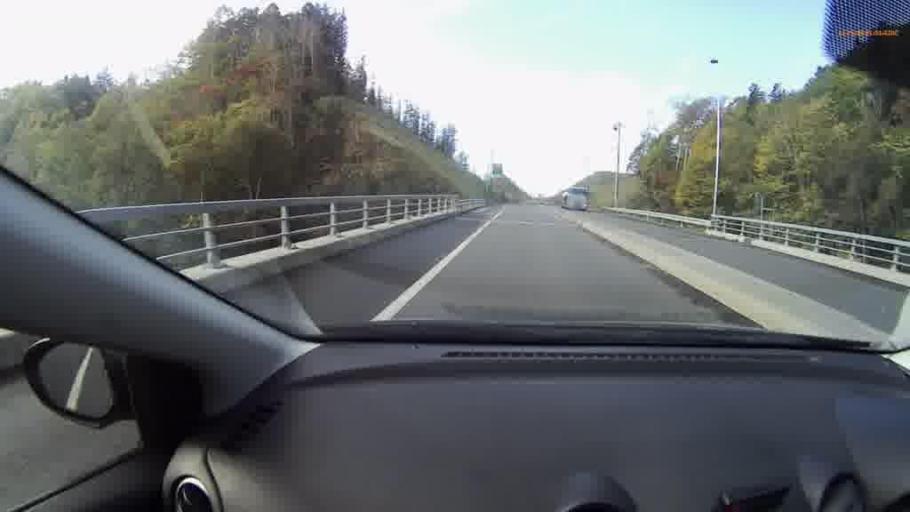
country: JP
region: Hokkaido
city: Kushiro
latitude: 43.0059
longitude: 144.5068
